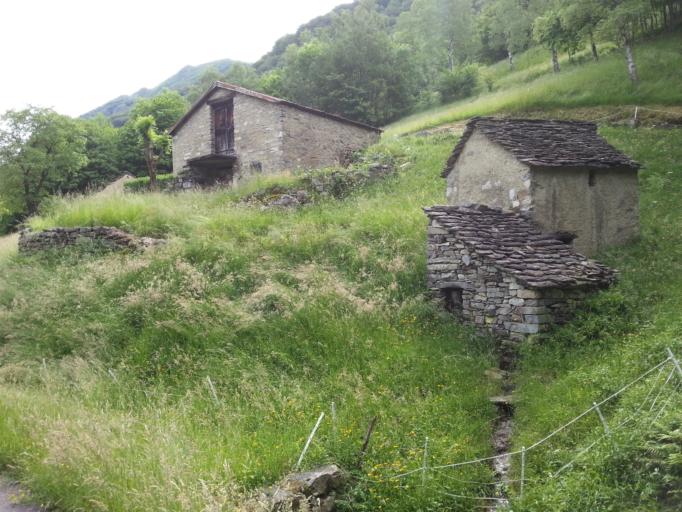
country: CH
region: Ticino
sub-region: Lugano District
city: Tesserete
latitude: 46.1108
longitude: 8.9731
